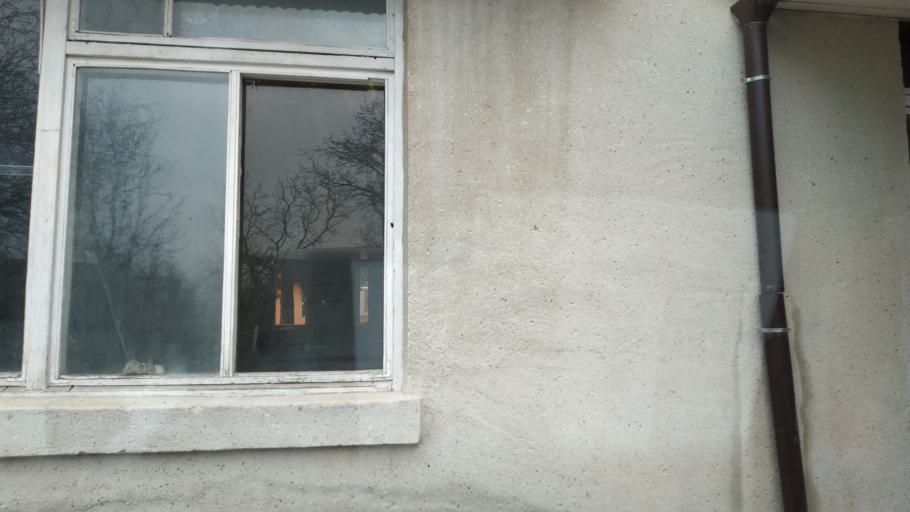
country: MD
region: Hincesti
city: Hincesti
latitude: 46.8896
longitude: 28.4113
